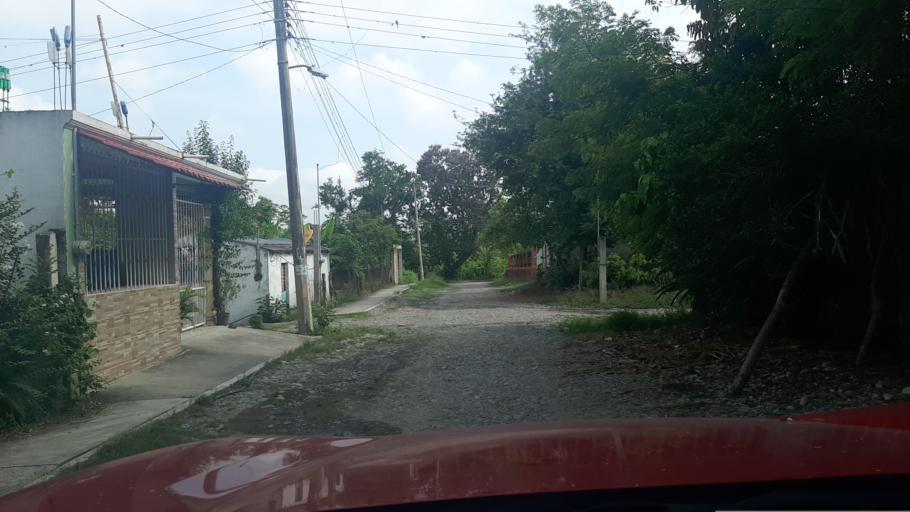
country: MX
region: Veracruz
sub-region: Coatzintla
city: Corralillos
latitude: 20.4846
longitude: -97.5024
